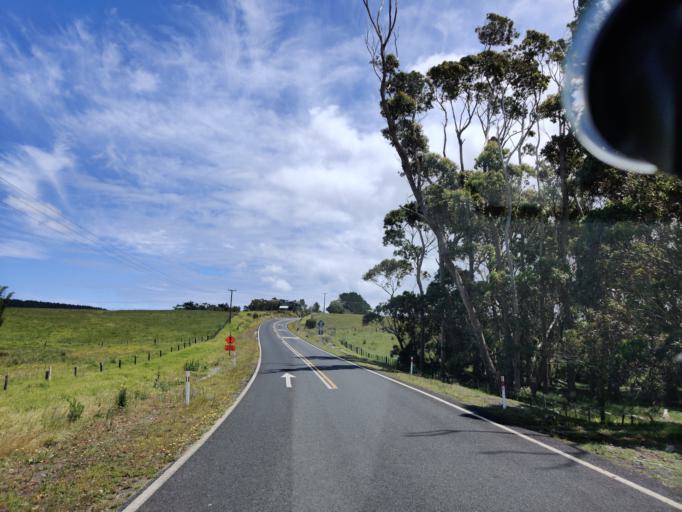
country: NZ
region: Northland
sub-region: Far North District
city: Kaitaia
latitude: -34.7078
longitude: 173.0338
